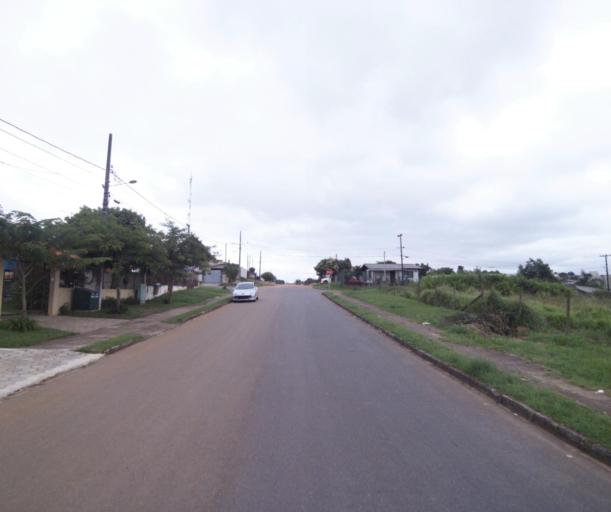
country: BR
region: Parana
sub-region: Quatro Barras
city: Quatro Barras
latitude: -25.3651
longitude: -49.1069
